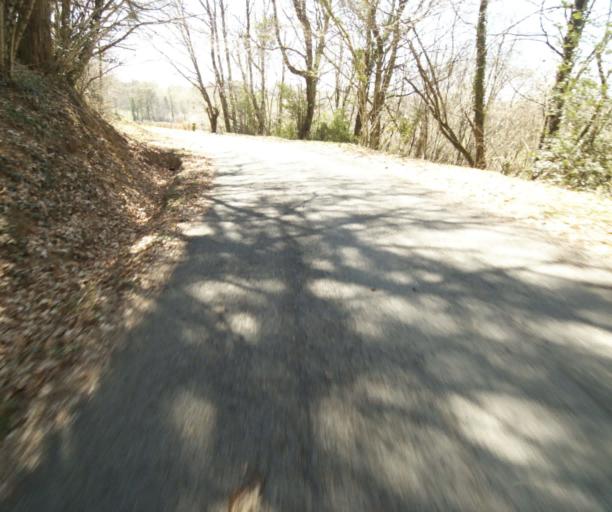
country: FR
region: Limousin
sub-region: Departement de la Correze
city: Seilhac
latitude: 45.3701
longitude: 1.7092
